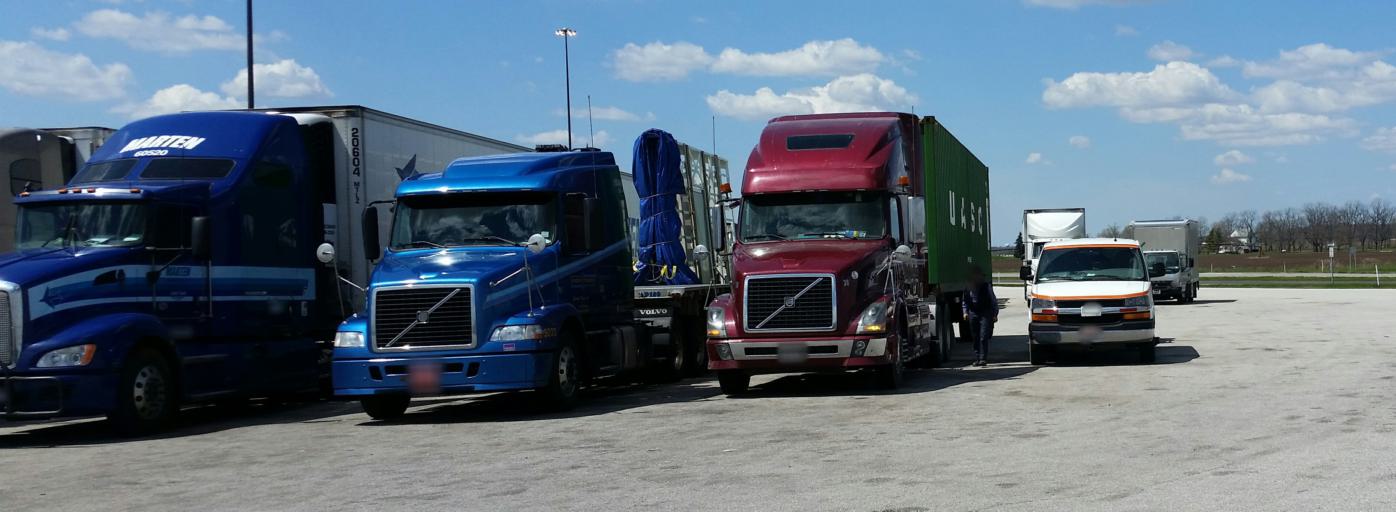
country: US
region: Michigan
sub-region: Saint Joseph County
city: Sturgis
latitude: 41.7454
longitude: -85.3299
